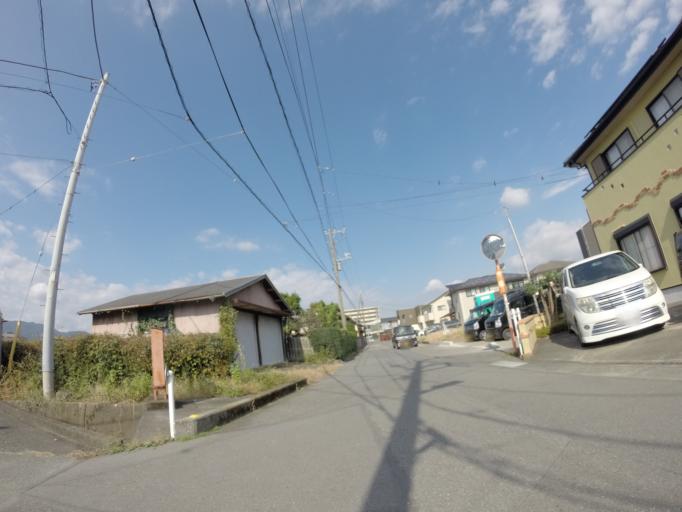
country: JP
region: Shizuoka
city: Fuji
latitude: 35.1395
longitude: 138.6606
